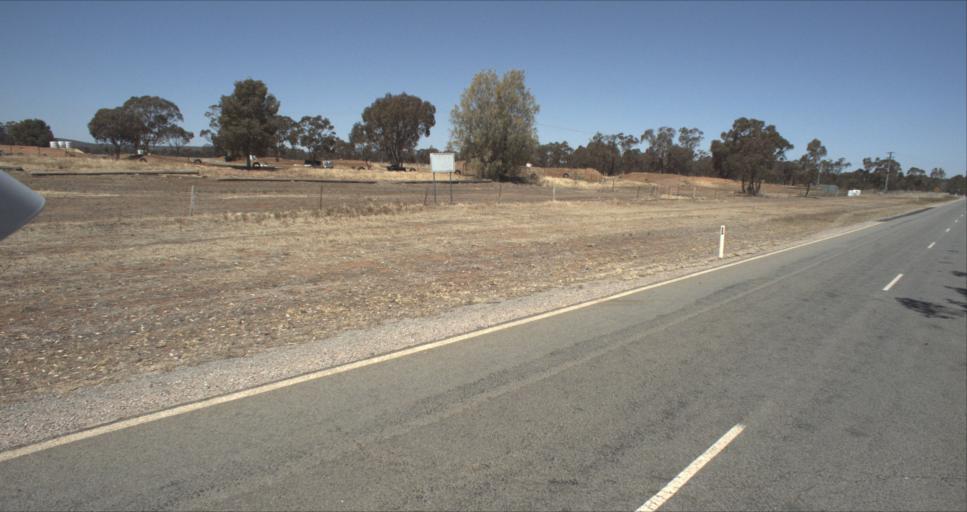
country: AU
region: New South Wales
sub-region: Leeton
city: Leeton
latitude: -34.5024
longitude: 146.4339
